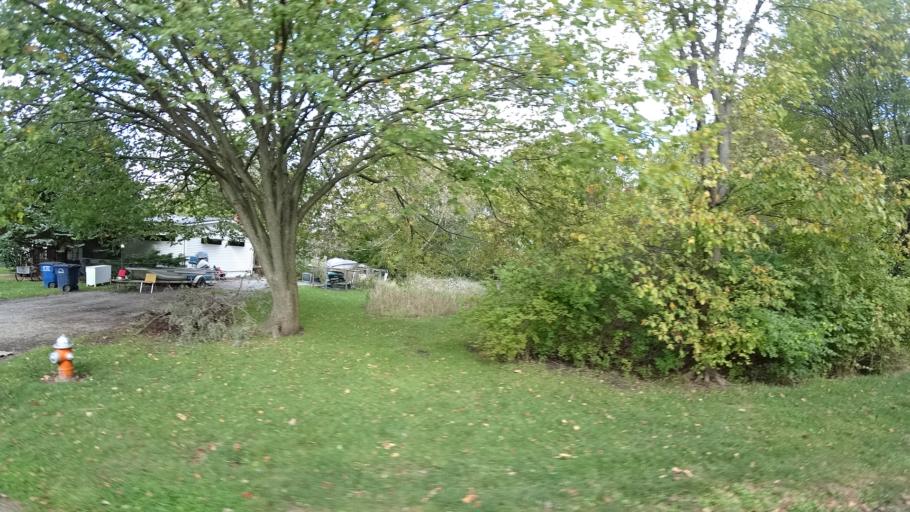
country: US
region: Indiana
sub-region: LaPorte County
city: Michigan City
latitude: 41.6707
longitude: -86.8977
